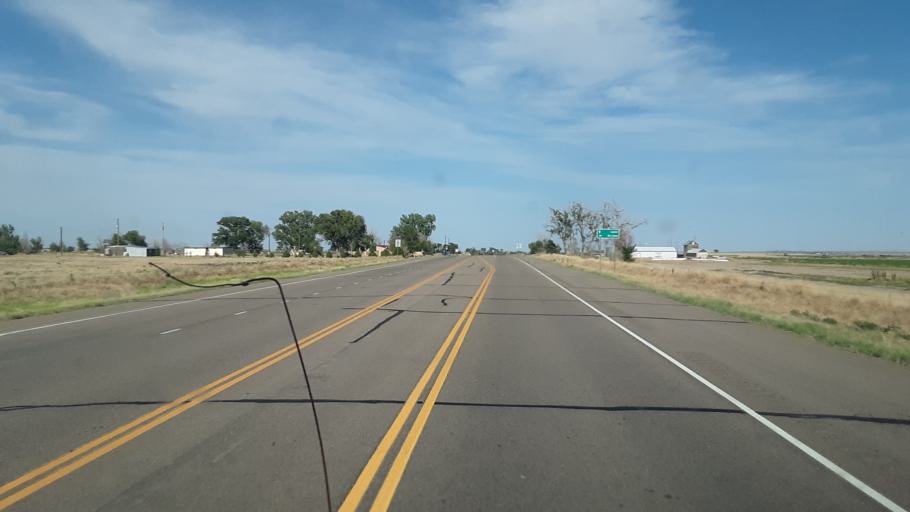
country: US
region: Colorado
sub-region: Prowers County
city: Lamar
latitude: 38.1141
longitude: -102.8553
